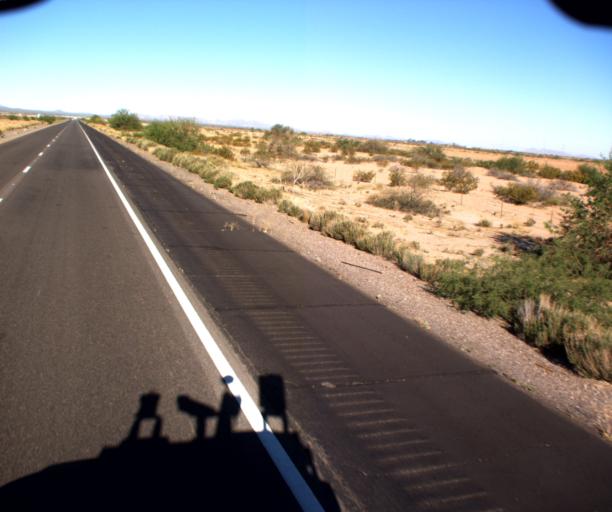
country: US
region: Arizona
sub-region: Pinal County
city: Casa Grande
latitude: 32.8284
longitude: -111.9249
